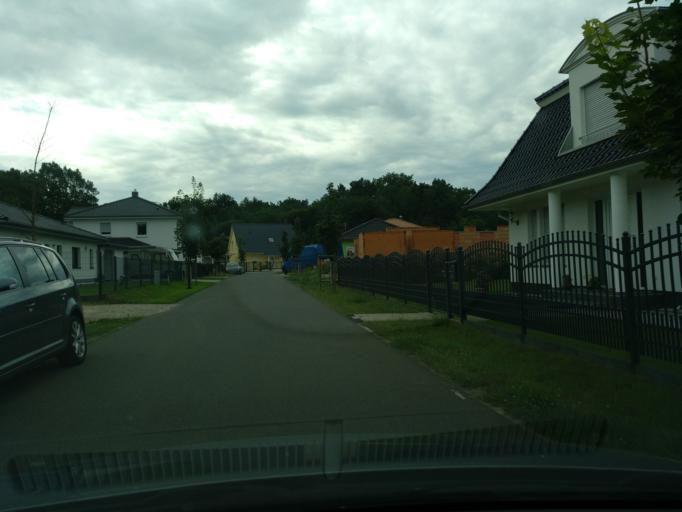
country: DE
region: Brandenburg
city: Bad Saarow
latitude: 52.2750
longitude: 14.0685
